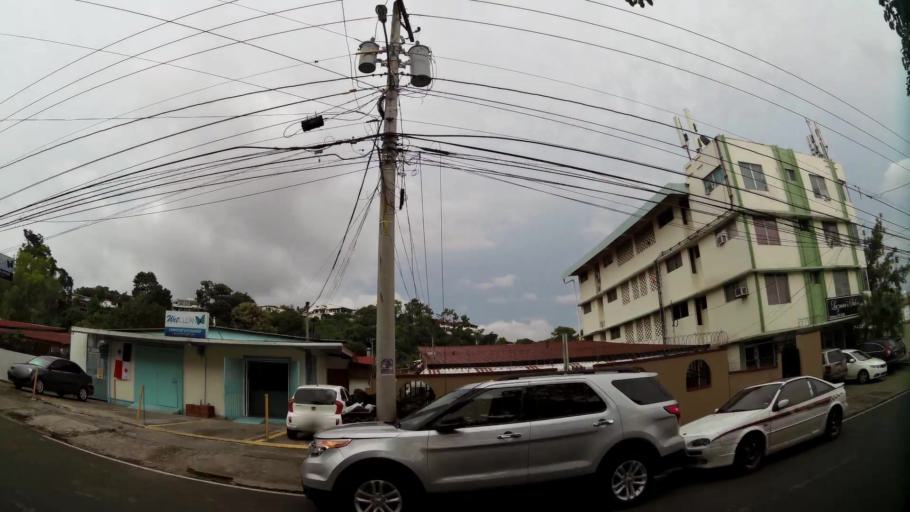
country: PA
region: Panama
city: Panama
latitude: 9.0112
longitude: -79.5265
